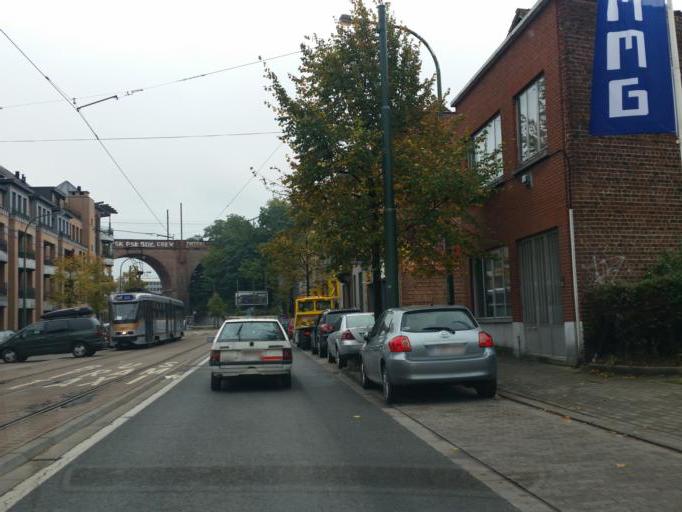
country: BE
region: Flanders
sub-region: Provincie Vlaams-Brabant
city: Drogenbos
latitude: 50.7962
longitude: 4.3262
